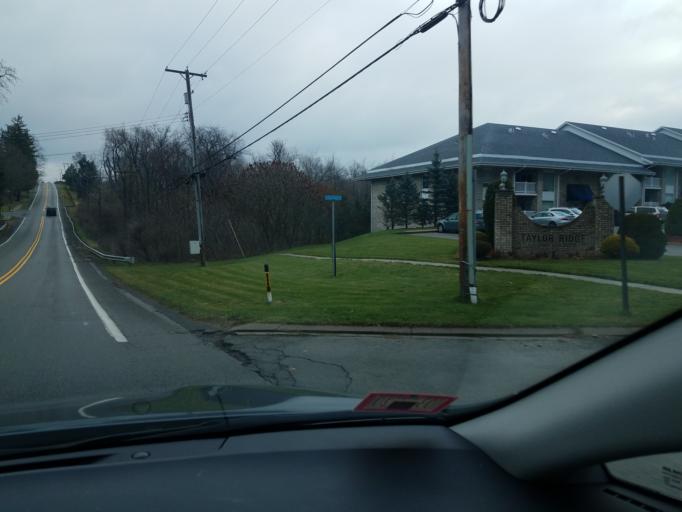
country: US
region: Pennsylvania
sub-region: Allegheny County
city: Franklin Park
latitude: 40.5946
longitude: -80.1002
